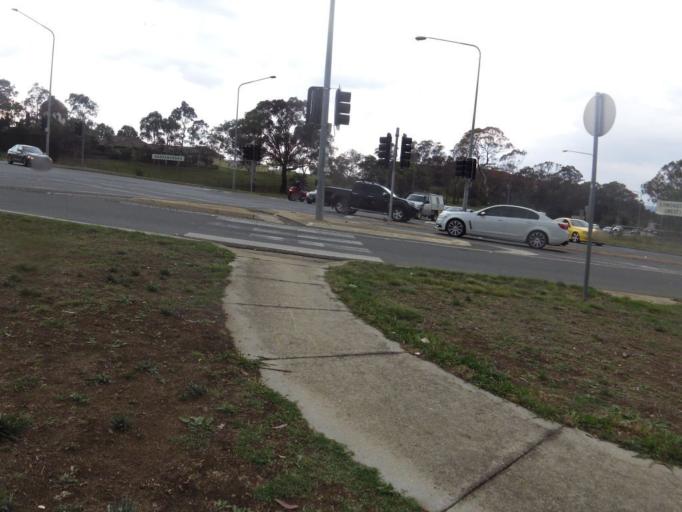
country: AU
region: Australian Capital Territory
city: Forrest
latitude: -35.3446
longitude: 149.1385
